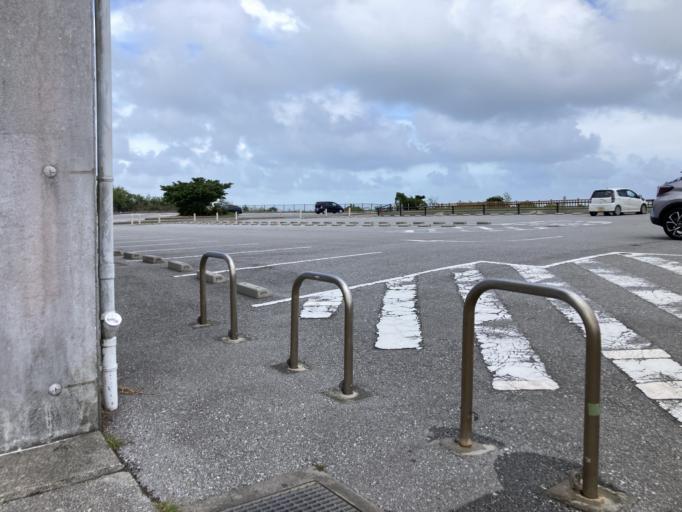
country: JP
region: Okinawa
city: Ginowan
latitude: 26.1675
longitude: 127.8289
